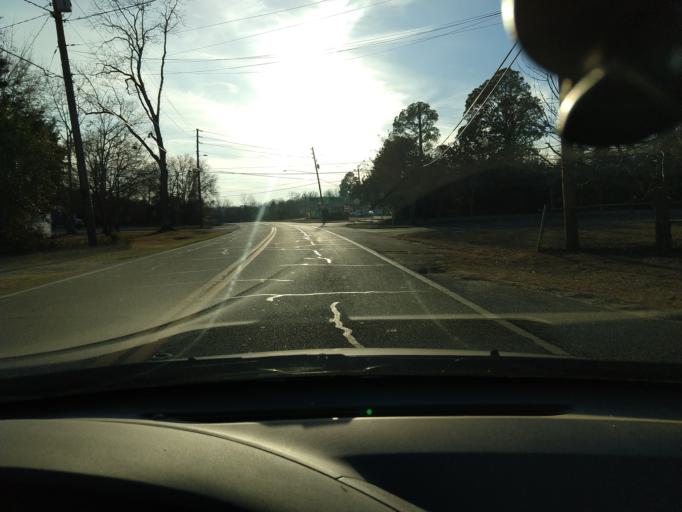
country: US
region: Georgia
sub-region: Sumter County
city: Americus
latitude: 32.0797
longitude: -84.2116
